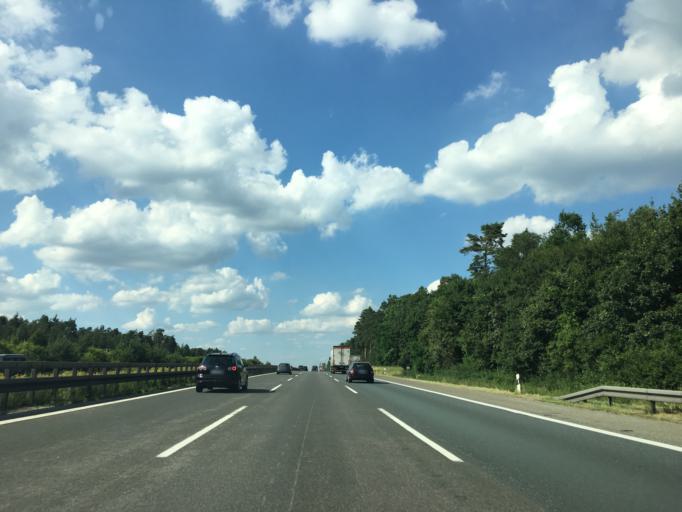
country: DE
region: Bavaria
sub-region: Regierungsbezirk Mittelfranken
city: Allersberg
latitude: 49.2995
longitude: 11.2083
